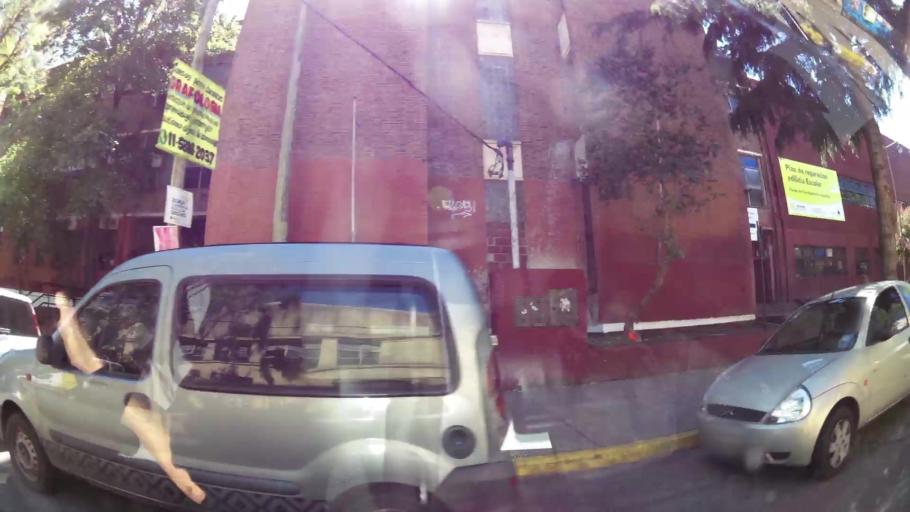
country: AR
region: Buenos Aires
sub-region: Partido de Quilmes
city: Quilmes
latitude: -34.7170
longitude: -58.2571
